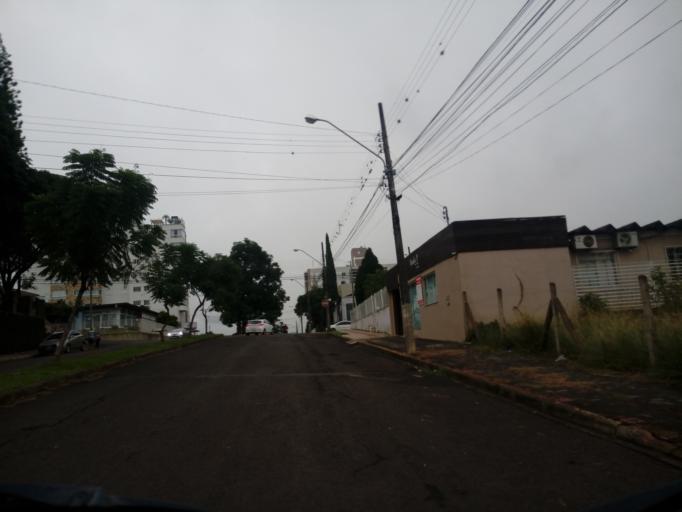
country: BR
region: Santa Catarina
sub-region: Chapeco
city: Chapeco
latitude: -27.1048
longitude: -52.6229
